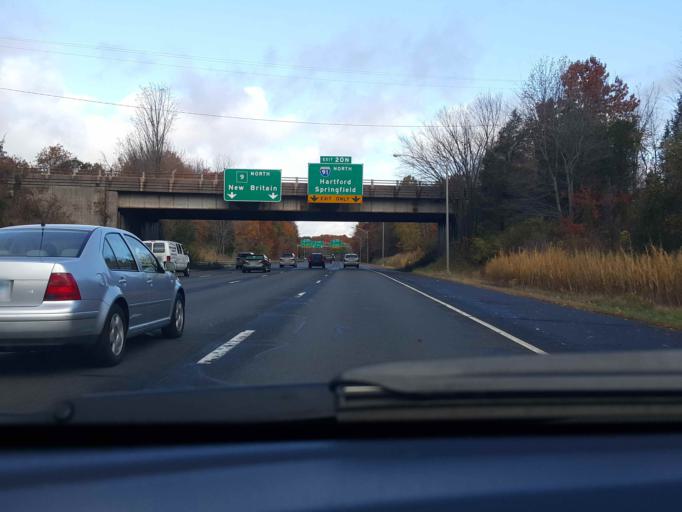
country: US
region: Connecticut
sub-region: Middlesex County
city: Cromwell
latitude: 41.6204
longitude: -72.6832
